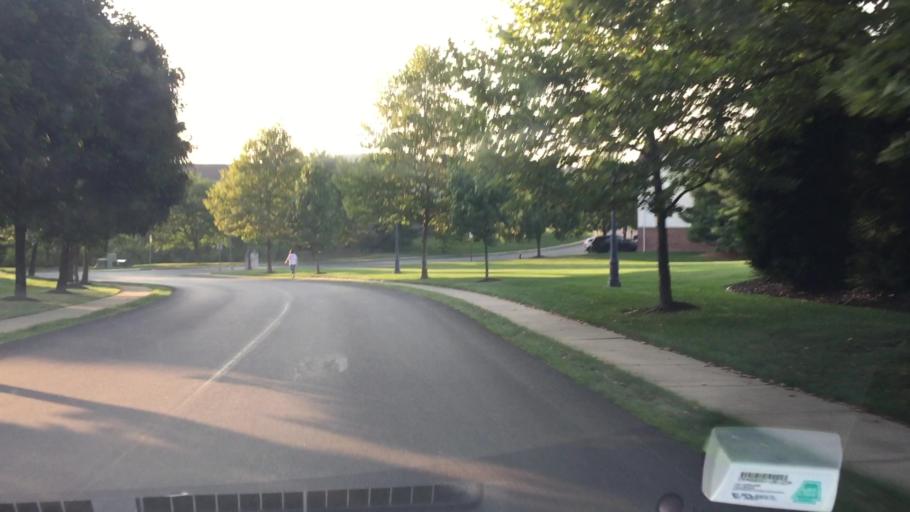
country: US
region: Pennsylvania
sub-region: Butler County
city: Seven Fields
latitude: 40.6819
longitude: -80.0464
